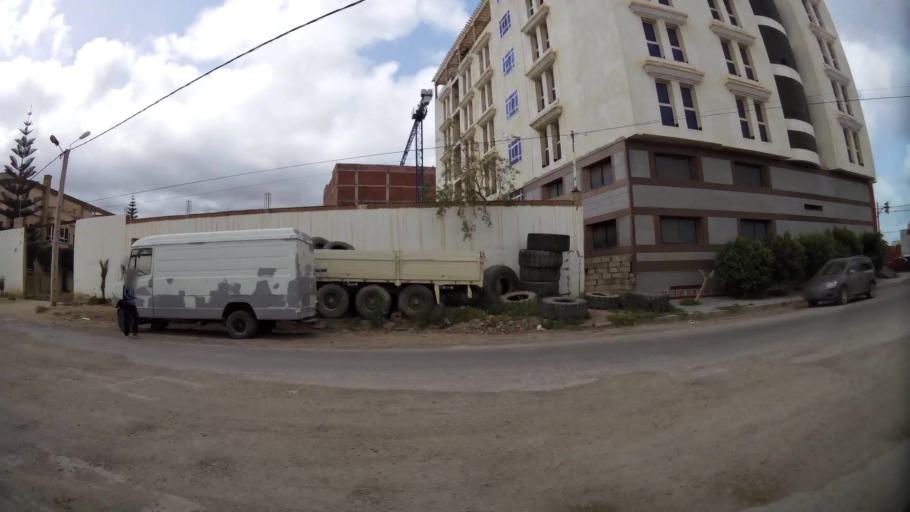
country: MA
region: Oriental
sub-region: Nador
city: Nador
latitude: 35.1584
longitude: -2.9308
